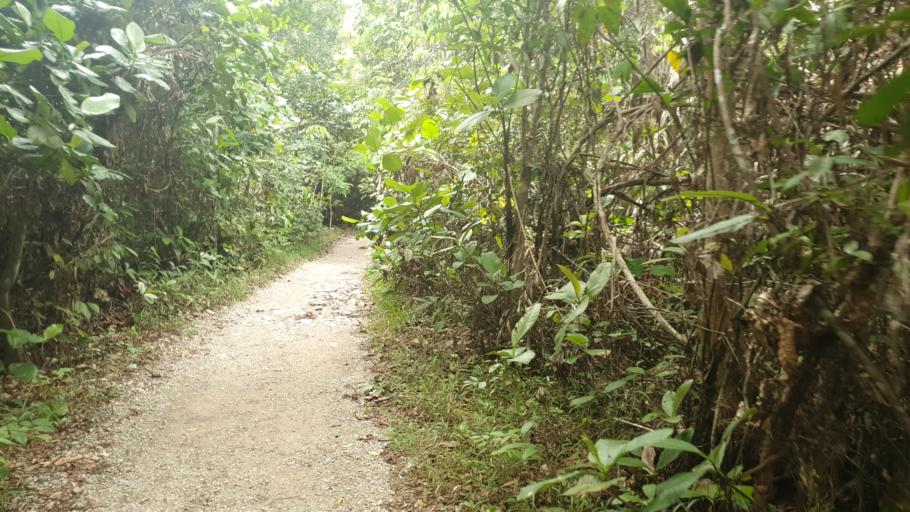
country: SG
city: Singapore
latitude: 1.3532
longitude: 103.8073
